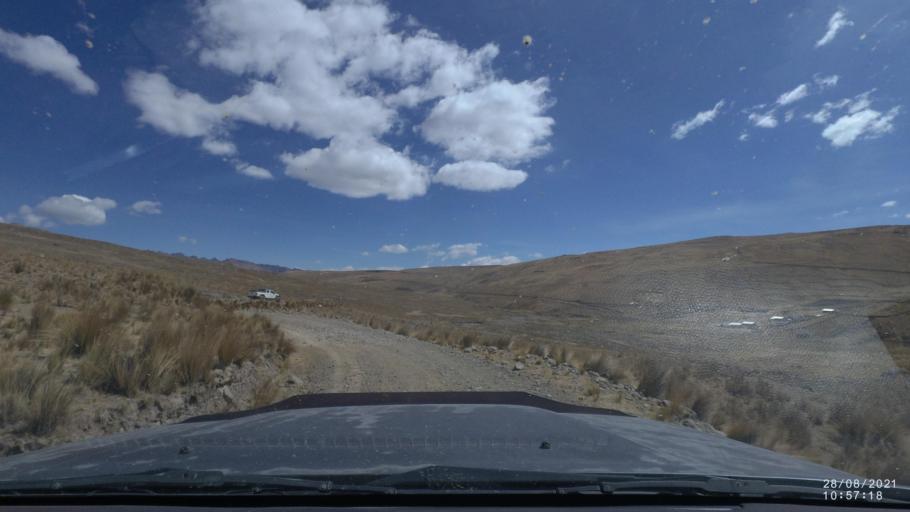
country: BO
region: Cochabamba
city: Cochabamba
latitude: -17.1886
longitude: -66.2509
